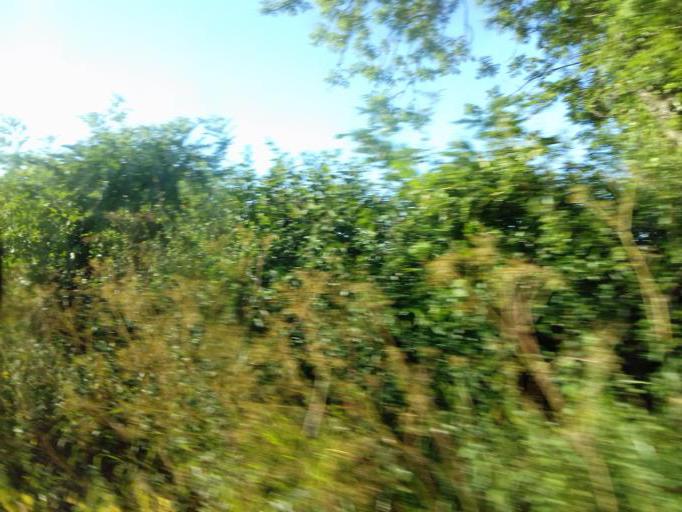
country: IE
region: Leinster
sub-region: Fingal County
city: Blanchardstown
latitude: 53.4518
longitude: -6.3398
